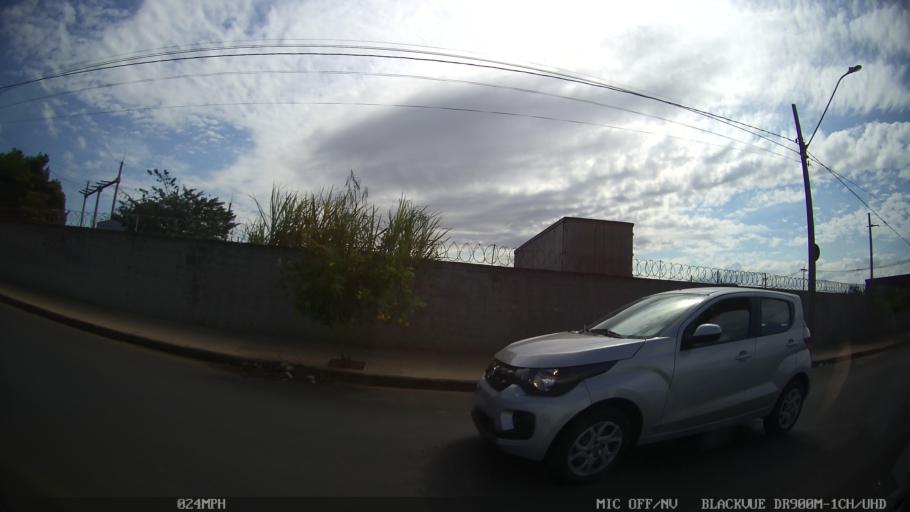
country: BR
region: Sao Paulo
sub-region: Americana
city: Americana
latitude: -22.7216
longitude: -47.3193
